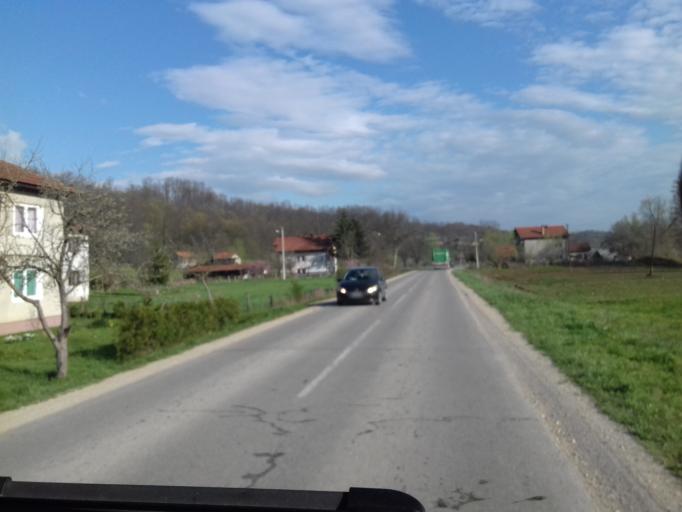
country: BA
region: Federation of Bosnia and Herzegovina
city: Tesanjka
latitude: 44.6504
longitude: 18.0172
